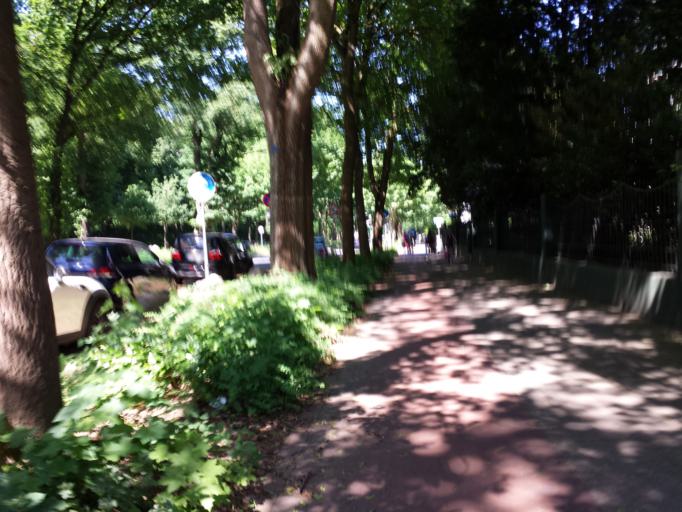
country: DE
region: Bremen
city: Bremen
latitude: 53.0892
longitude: 8.8297
